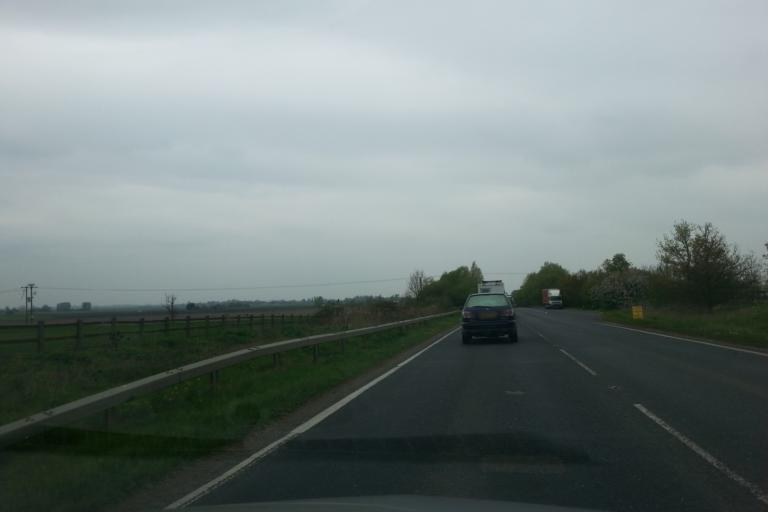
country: GB
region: England
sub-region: Cambridgeshire
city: Littleport
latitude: 52.4505
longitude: 0.2836
